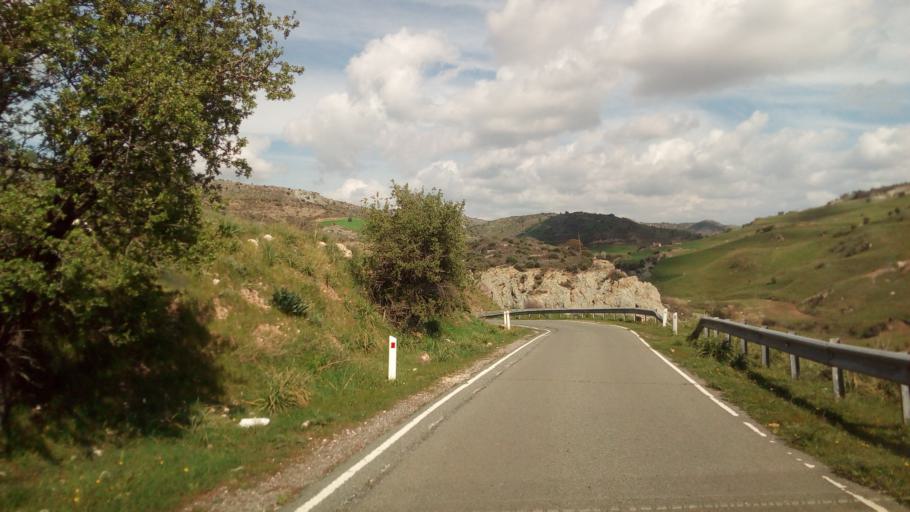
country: CY
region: Pafos
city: Mesogi
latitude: 34.7599
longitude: 32.5519
